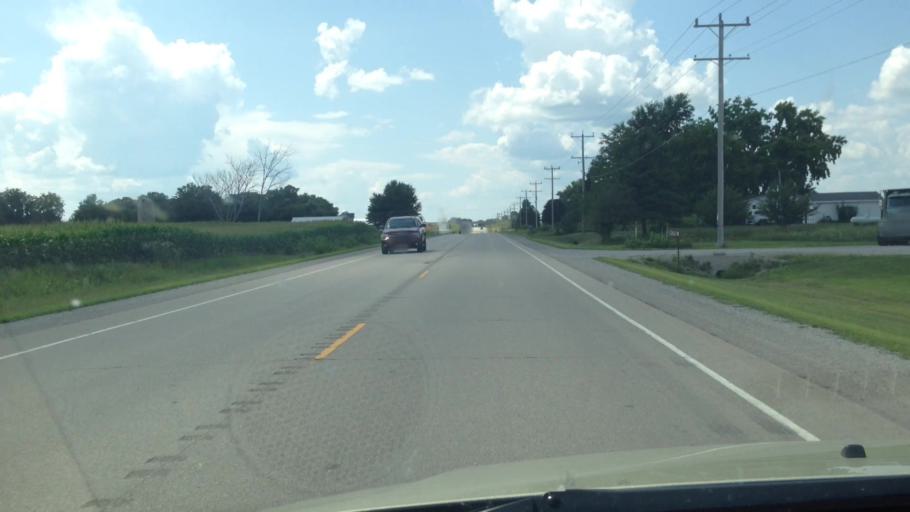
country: US
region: Wisconsin
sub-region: Brown County
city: Pulaski
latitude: 44.6735
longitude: -88.2945
